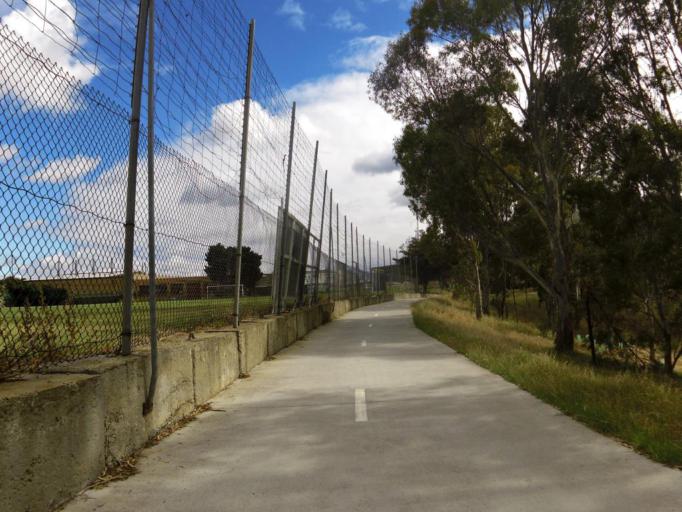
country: AU
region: Victoria
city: Heidelberg West
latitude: -37.7580
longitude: 145.0286
